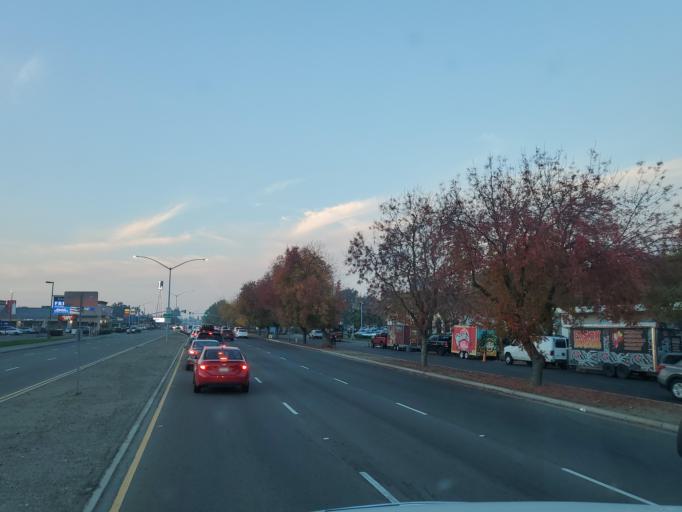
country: US
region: California
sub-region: San Joaquin County
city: Lincoln Village
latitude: 38.0091
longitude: -121.3198
